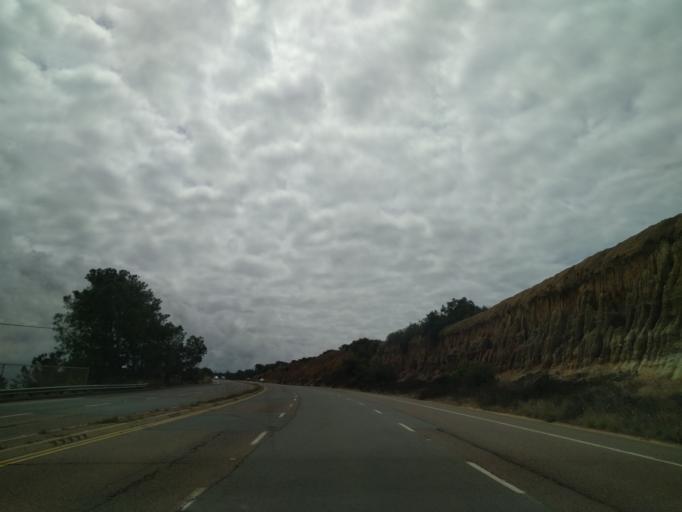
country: US
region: California
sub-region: San Diego County
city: Del Mar
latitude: 32.9180
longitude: -117.2486
